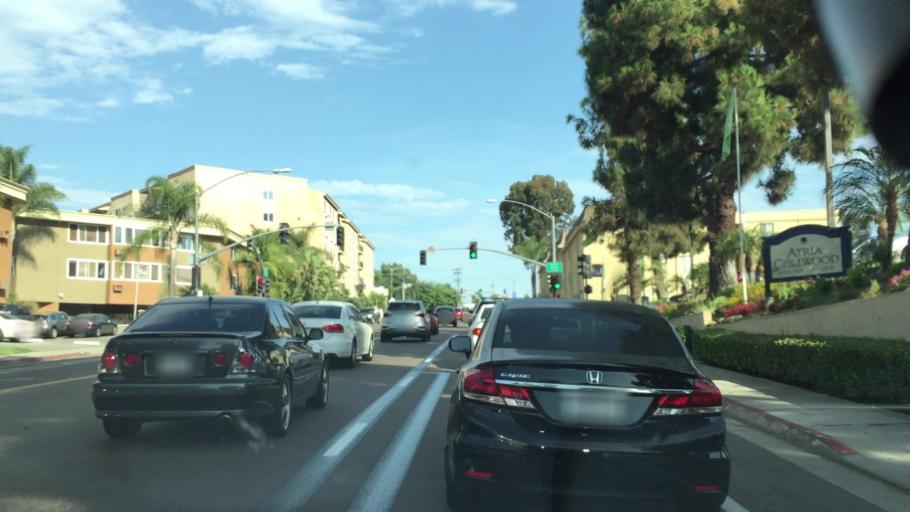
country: US
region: California
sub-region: San Diego County
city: Lemon Grove
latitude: 32.7603
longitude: -117.0812
